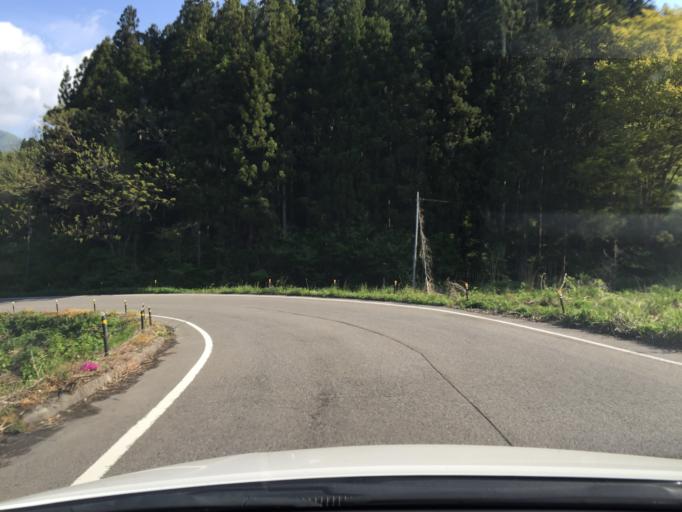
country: JP
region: Fukushima
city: Kitakata
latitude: 37.6855
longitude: 139.6752
